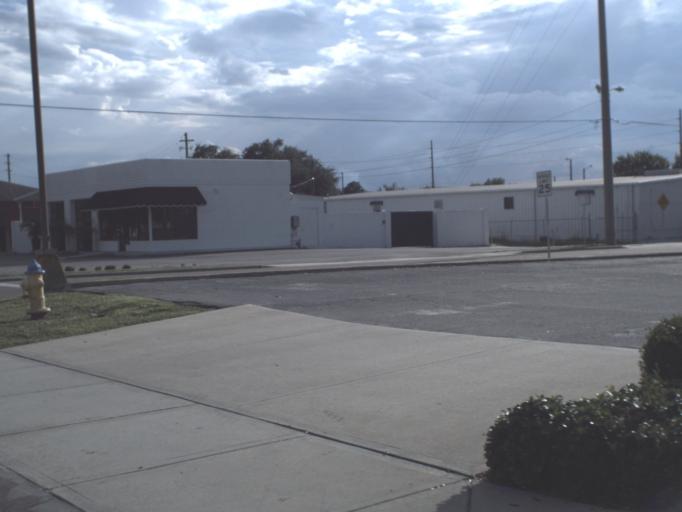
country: US
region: Florida
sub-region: Polk County
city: Winter Haven
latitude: 28.0170
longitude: -81.7308
